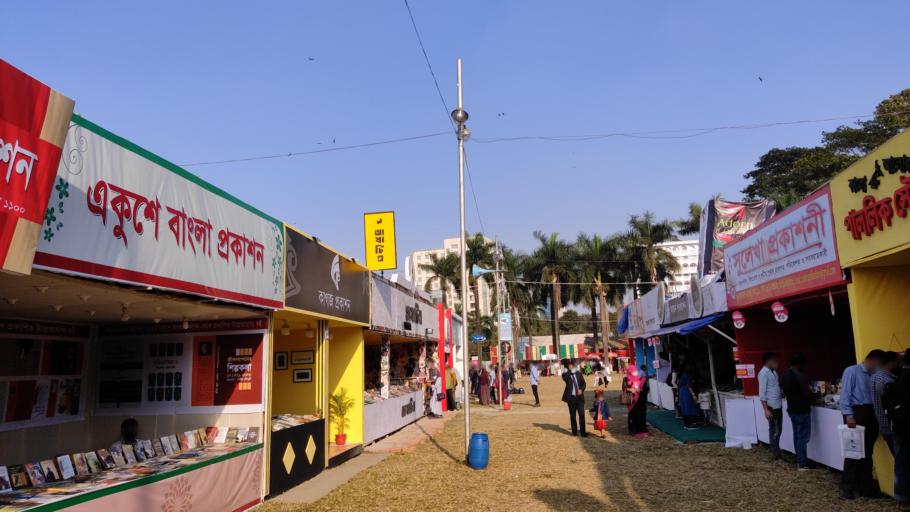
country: BD
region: Dhaka
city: Azimpur
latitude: 23.7322
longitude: 90.3984
